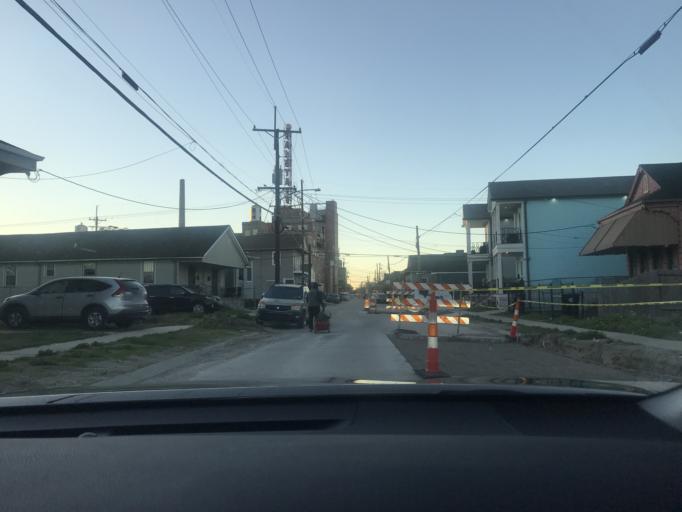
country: US
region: Louisiana
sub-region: Orleans Parish
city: New Orleans
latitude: 29.9592
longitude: -90.0883
